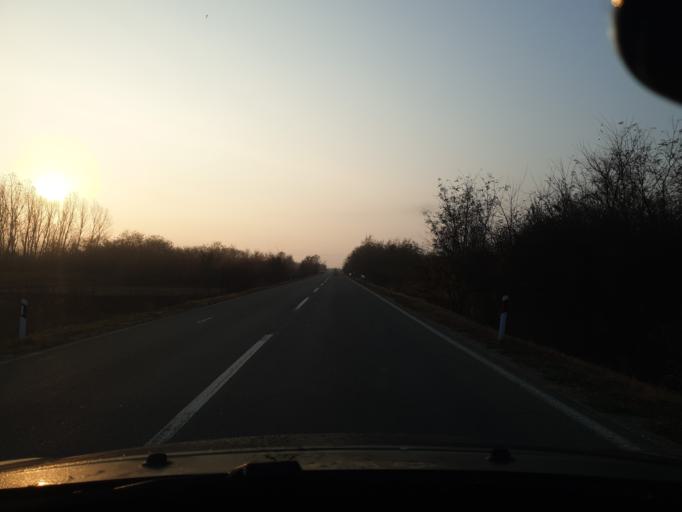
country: RS
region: Central Serbia
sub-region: Jablanicki Okrug
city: Leskovac
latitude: 42.9586
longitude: 21.9849
